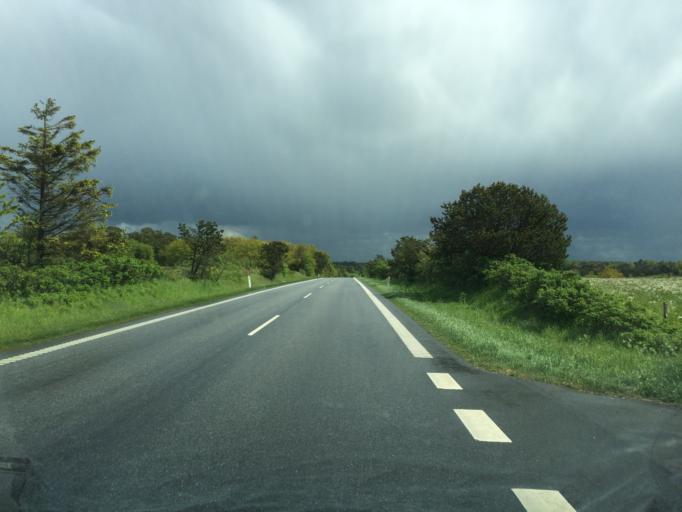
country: DK
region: Central Jutland
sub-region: Skive Kommune
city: Hojslev
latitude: 56.6039
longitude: 9.2586
